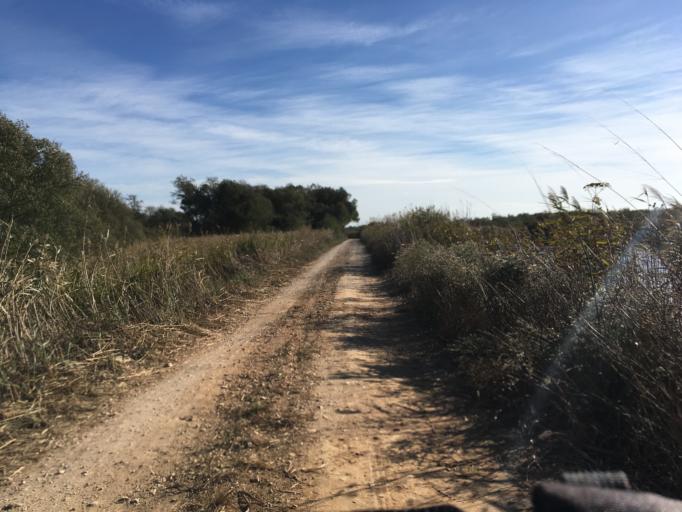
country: PT
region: Aveiro
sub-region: Estarreja
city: Salreu
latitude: 40.7170
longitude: -8.5757
